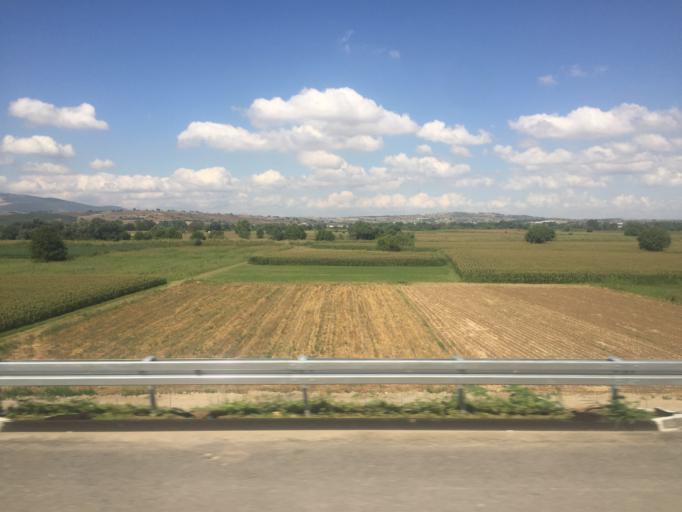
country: TR
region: Balikesir
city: Gobel
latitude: 40.0043
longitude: 28.1945
